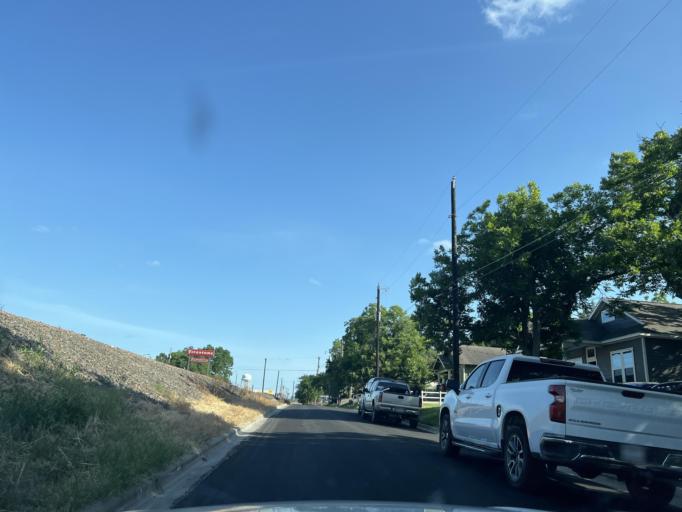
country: US
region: Texas
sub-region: Washington County
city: Brenham
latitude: 30.1689
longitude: -96.4008
